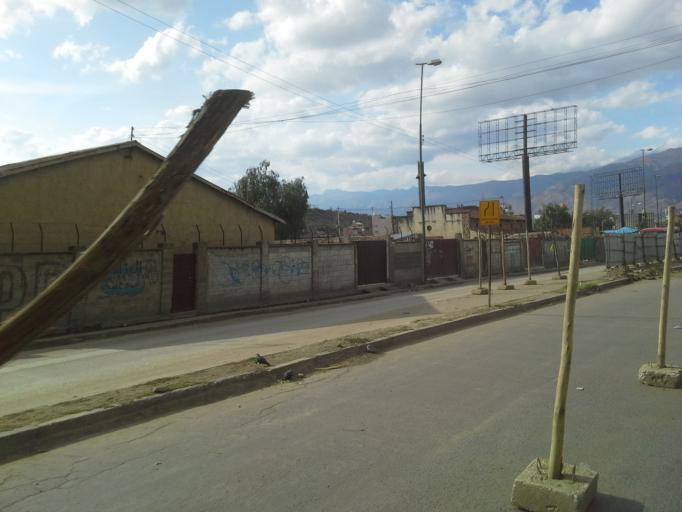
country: BO
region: Cochabamba
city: Cochabamba
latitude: -17.4136
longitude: -66.1537
